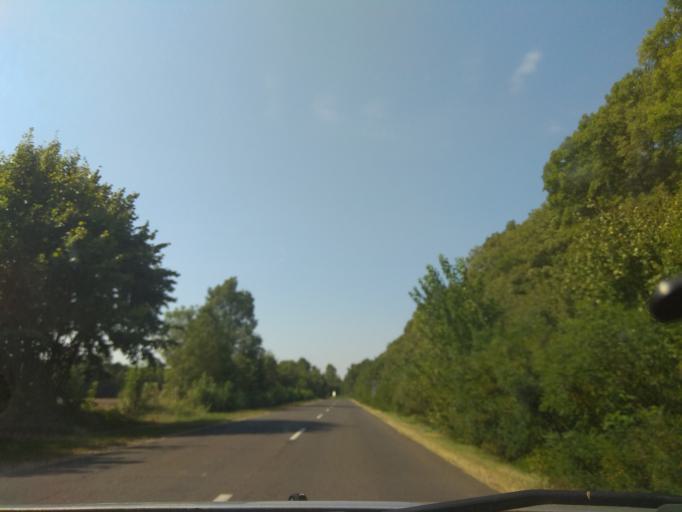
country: HU
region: Borsod-Abauj-Zemplen
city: Harsany
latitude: 47.9239
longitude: 20.7232
